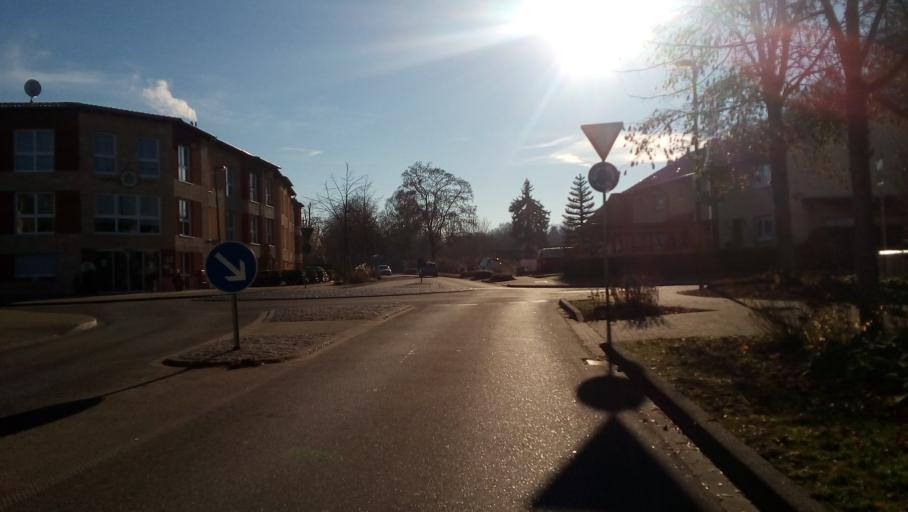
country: DE
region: Baden-Wuerttemberg
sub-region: Freiburg Region
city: Achern
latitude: 48.6278
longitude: 8.0799
